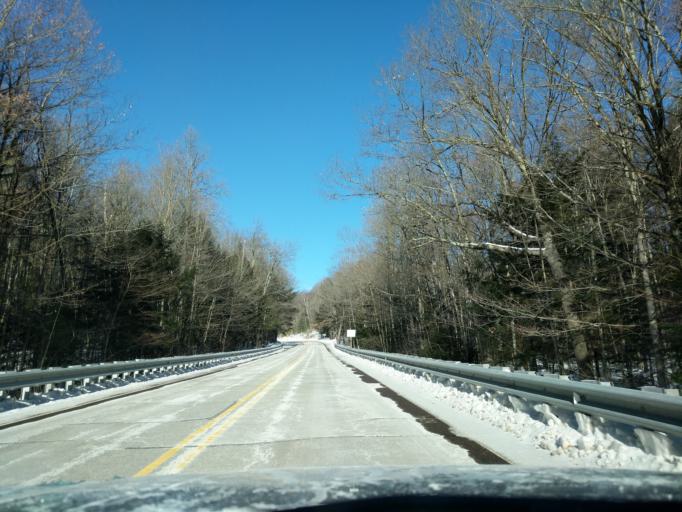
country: US
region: Wisconsin
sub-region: Menominee County
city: Keshena
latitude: 45.0955
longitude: -88.6340
